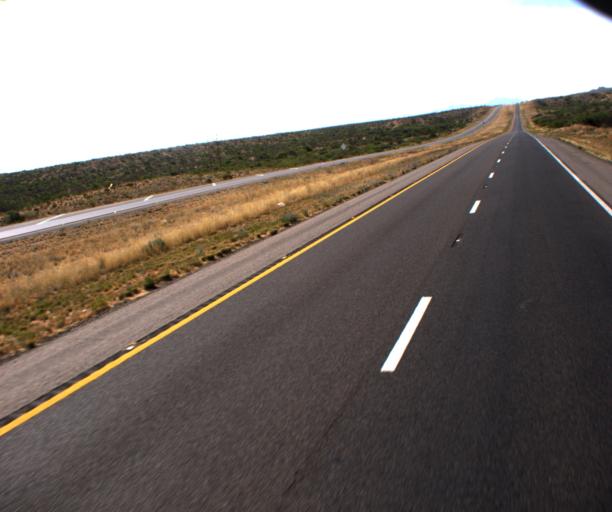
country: US
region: Arizona
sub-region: Graham County
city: Swift Trail Junction
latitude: 32.5900
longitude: -109.6841
